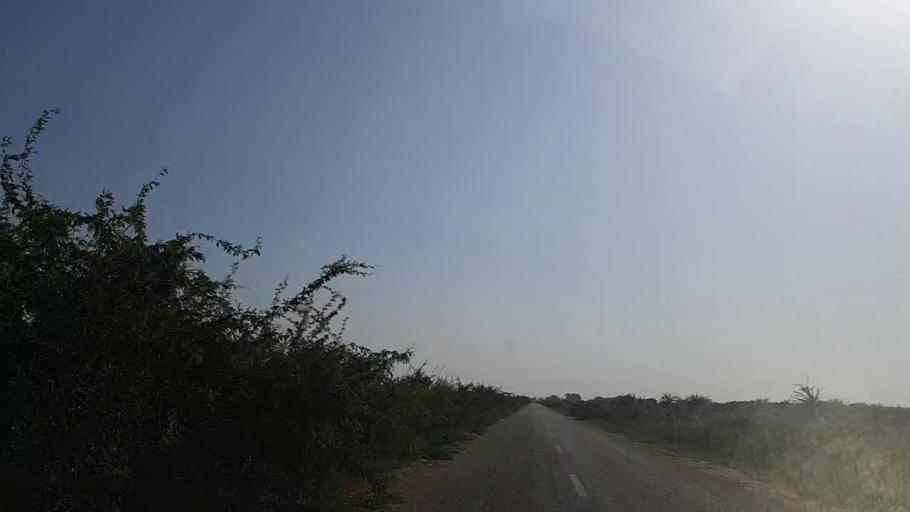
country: PK
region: Sindh
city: Jati
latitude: 24.4344
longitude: 68.2599
